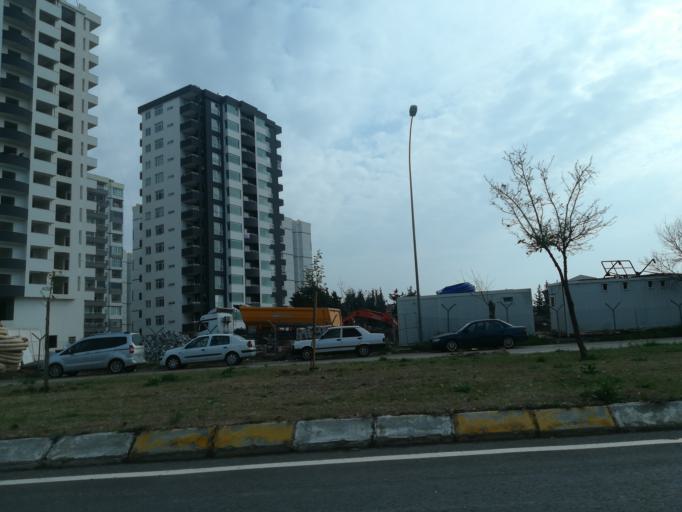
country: TR
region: Adana
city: Yuregir
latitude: 36.9875
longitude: 35.3671
